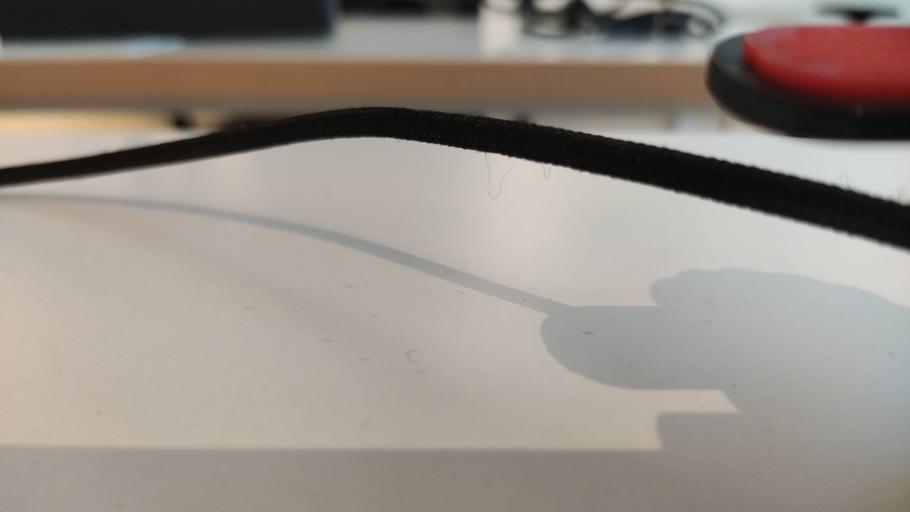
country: RU
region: Moskovskaya
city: Novopetrovskoye
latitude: 55.9411
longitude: 36.4358
